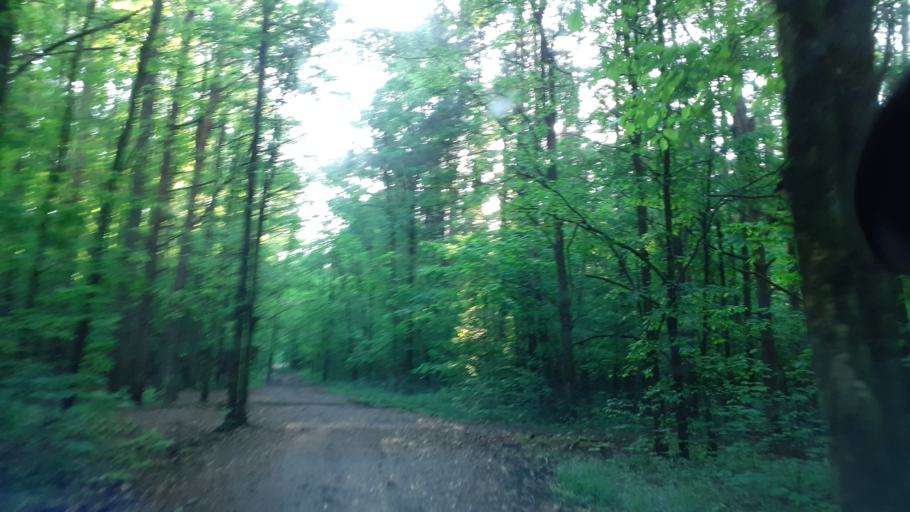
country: RU
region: Moskovskaya
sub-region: Podol'skiy Rayon
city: Podol'sk
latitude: 55.4601
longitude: 37.5309
